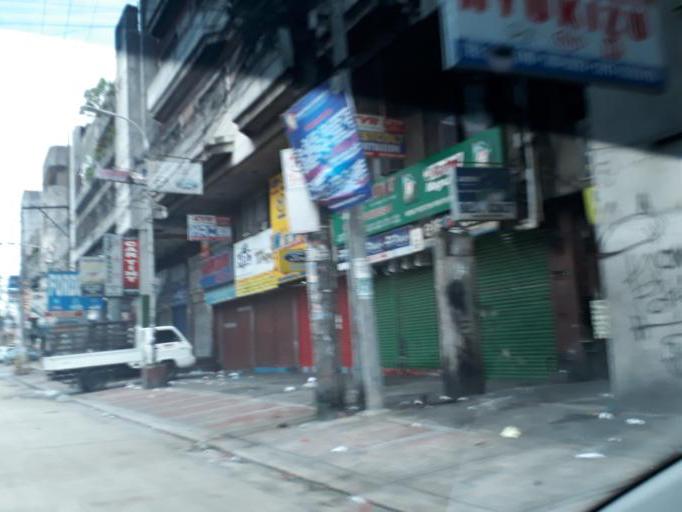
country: PH
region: Calabarzon
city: Del Monte
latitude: 14.6199
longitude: 121.0097
